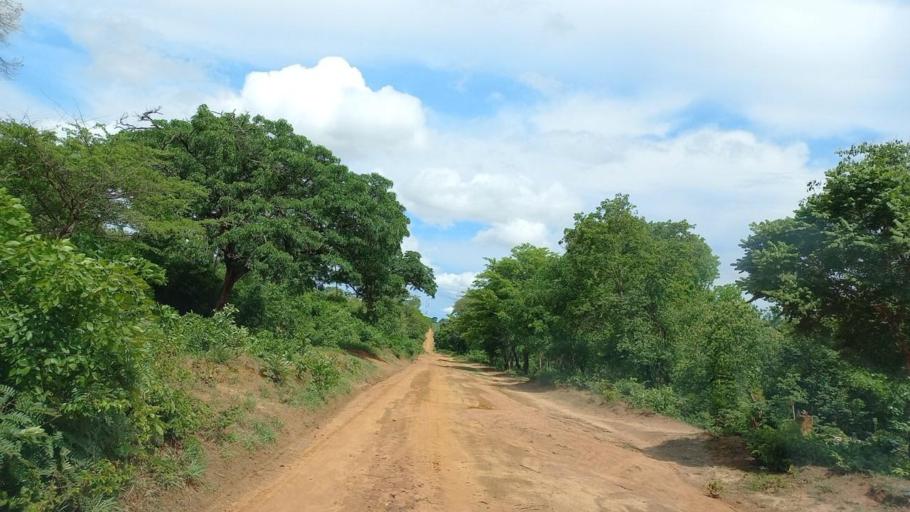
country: ZM
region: North-Western
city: Kabompo
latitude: -13.5440
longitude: 24.1017
